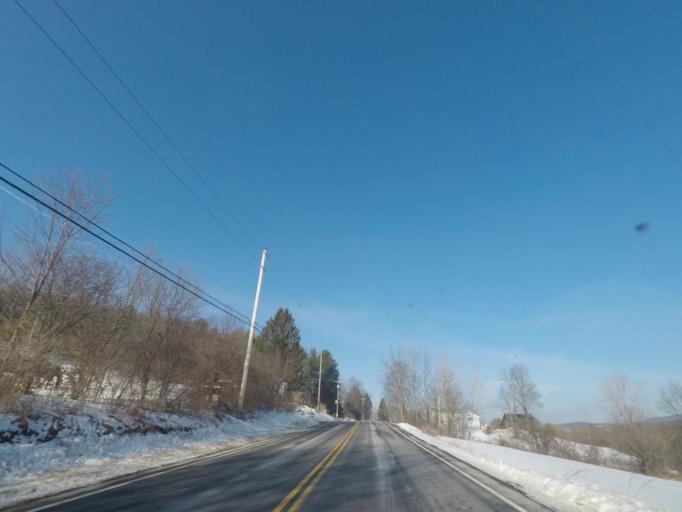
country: US
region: Massachusetts
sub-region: Berkshire County
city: Richmond
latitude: 42.4830
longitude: -73.3898
